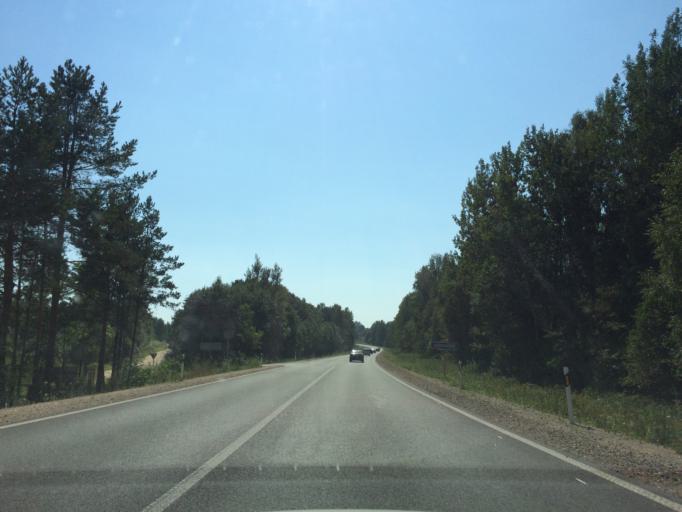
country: LV
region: Rezekne
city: Rezekne
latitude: 56.3674
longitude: 27.1848
